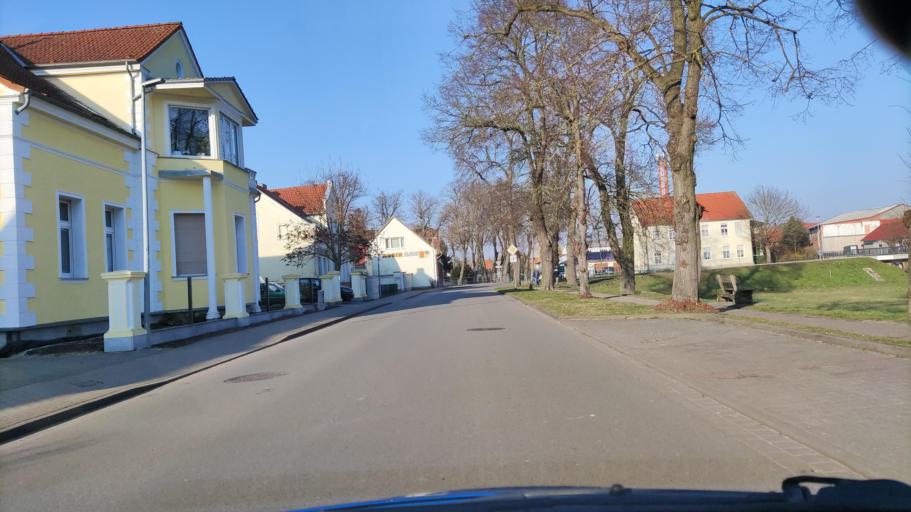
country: DE
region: Saxony-Anhalt
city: Seehausen
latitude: 52.8905
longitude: 11.7497
